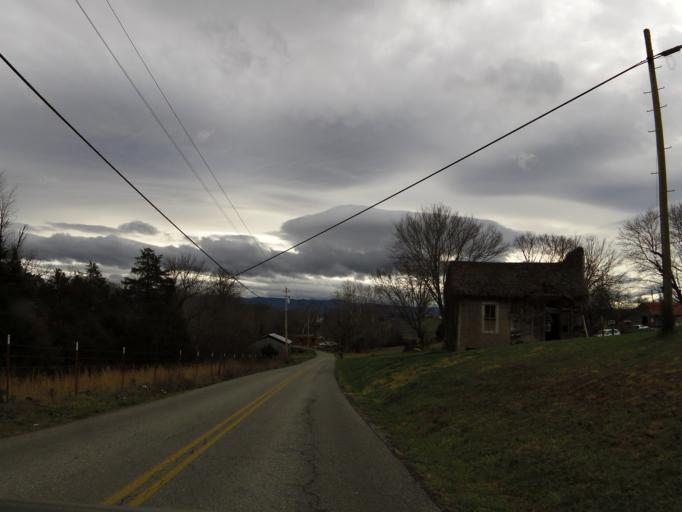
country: US
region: Tennessee
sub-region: Greene County
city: Tusculum
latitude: 36.2049
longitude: -82.7444
